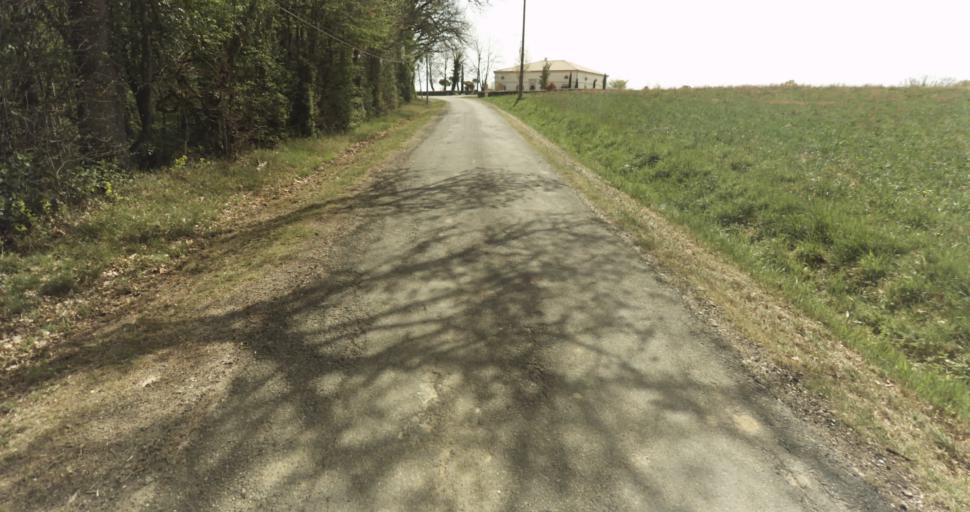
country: FR
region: Midi-Pyrenees
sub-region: Departement du Tarn-et-Garonne
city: Moissac
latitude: 44.1639
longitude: 1.0735
